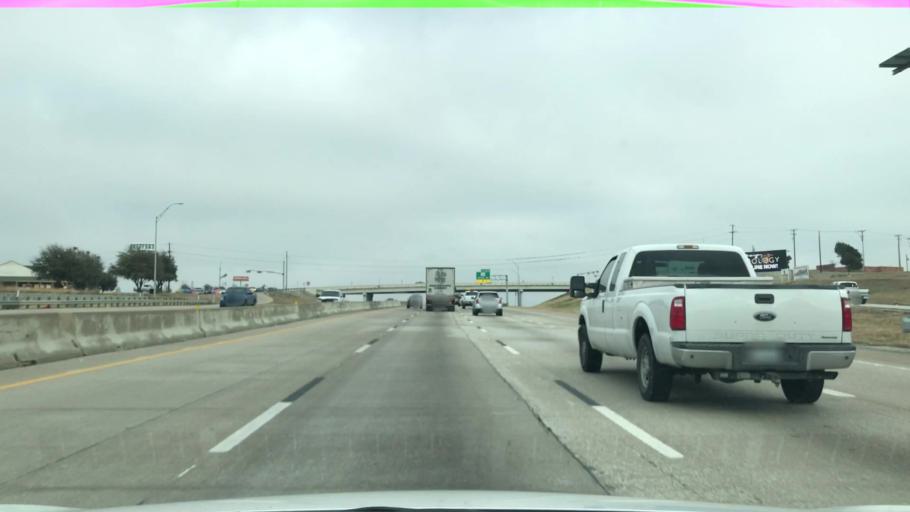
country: US
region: Texas
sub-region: Rockwall County
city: Rockwall
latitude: 32.8946
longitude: -96.4788
